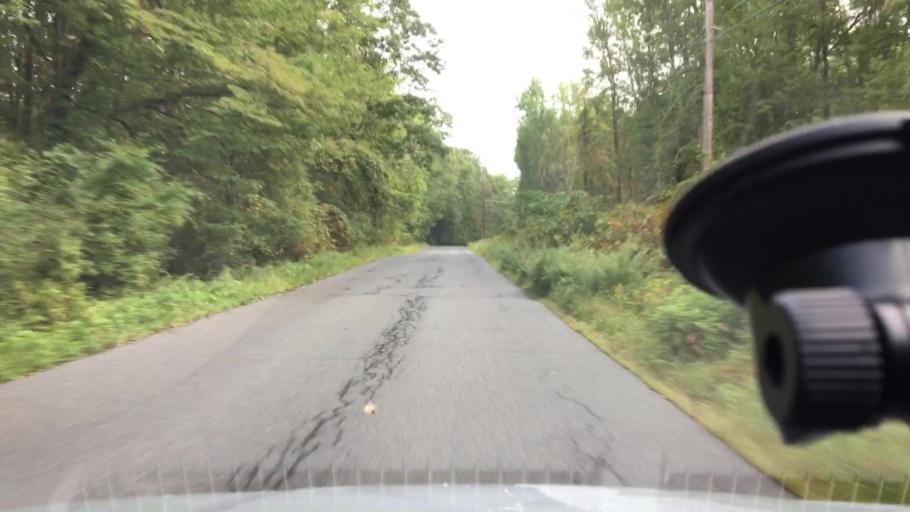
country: US
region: Pennsylvania
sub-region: Monroe County
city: Mountainhome
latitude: 41.1478
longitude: -75.2558
